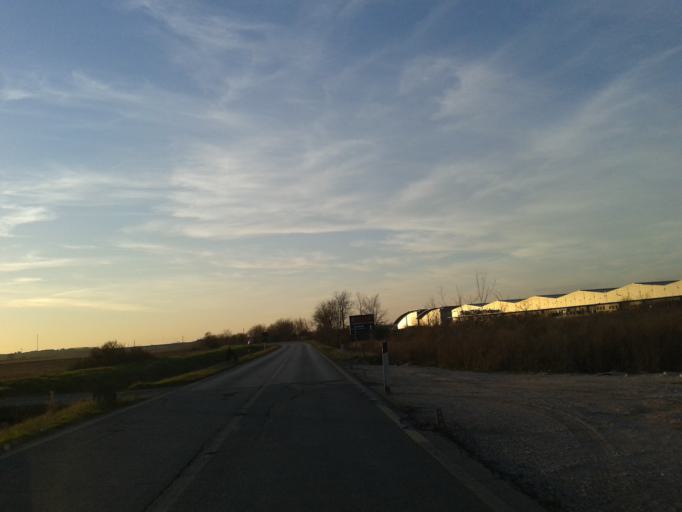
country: IT
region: Tuscany
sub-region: Provincia di Livorno
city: Guasticce
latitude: 43.5967
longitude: 10.3805
